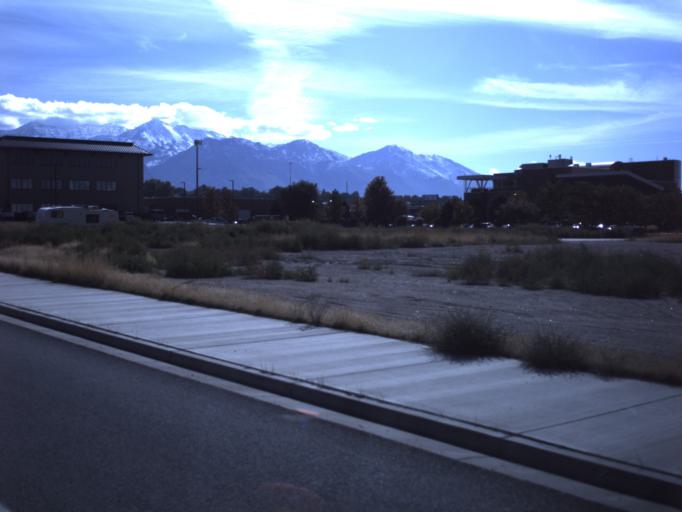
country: US
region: Utah
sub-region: Utah County
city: Lindon
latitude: 40.3118
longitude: -111.7324
